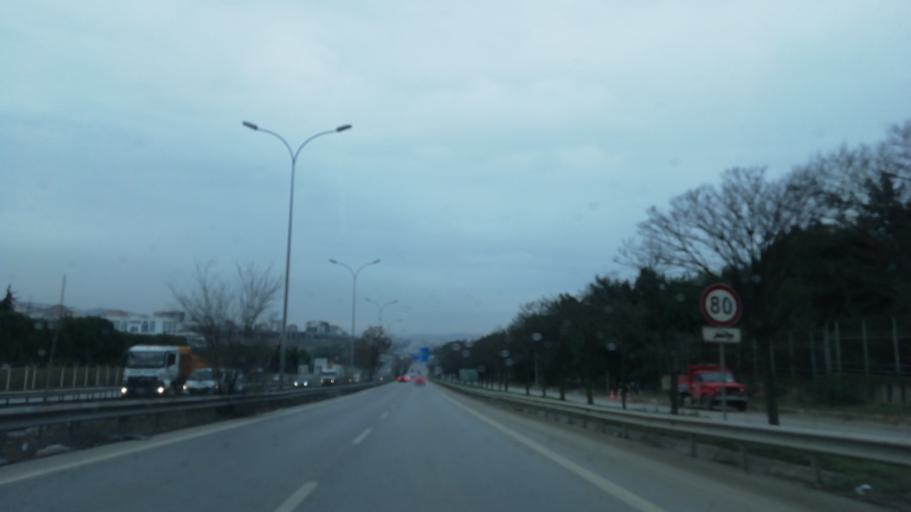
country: TR
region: Kocaeli
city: Darica
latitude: 40.8197
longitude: 29.3582
